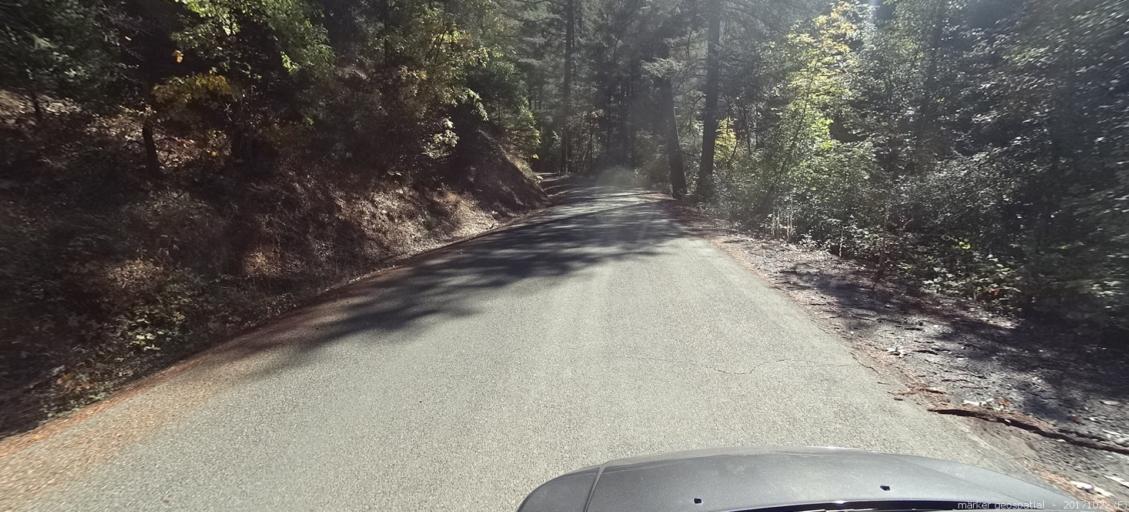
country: US
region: California
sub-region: Shasta County
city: Central Valley (historical)
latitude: 40.9300
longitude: -122.4884
